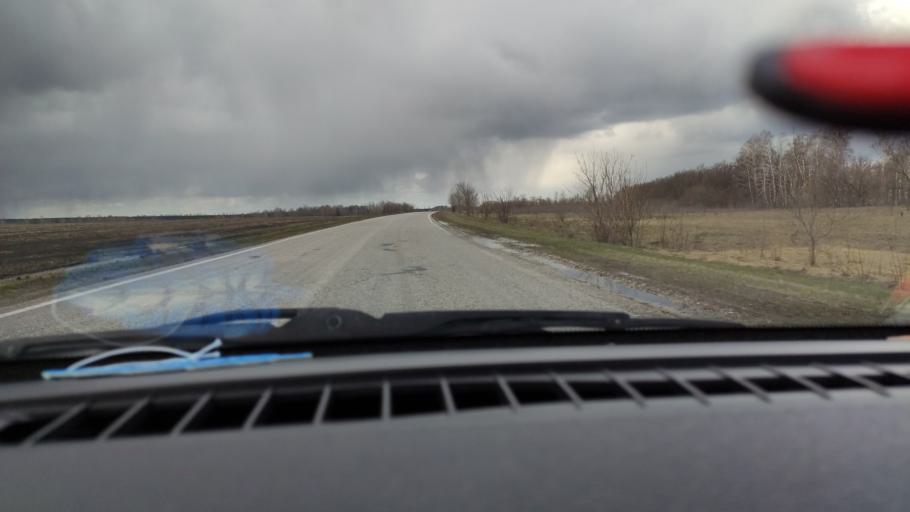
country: RU
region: Samara
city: Povolzhskiy
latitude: 53.7934
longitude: 49.7453
